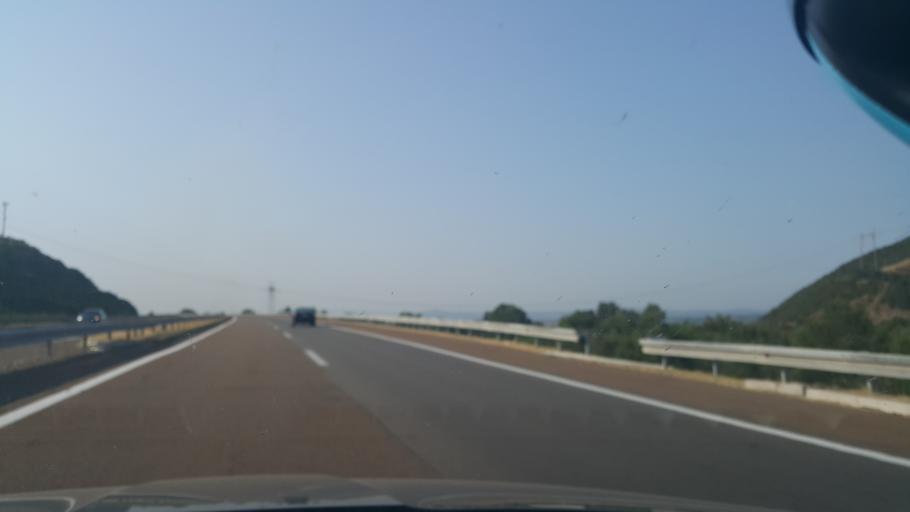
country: RS
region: Central Serbia
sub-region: Nisavski Okrug
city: Doljevac
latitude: 43.2151
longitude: 21.8361
